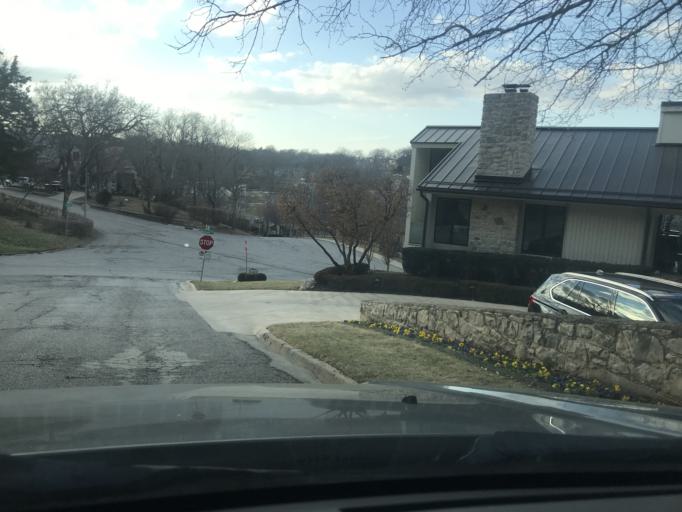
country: US
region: Kansas
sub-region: Johnson County
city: Westwood
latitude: 39.0379
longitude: -94.5958
